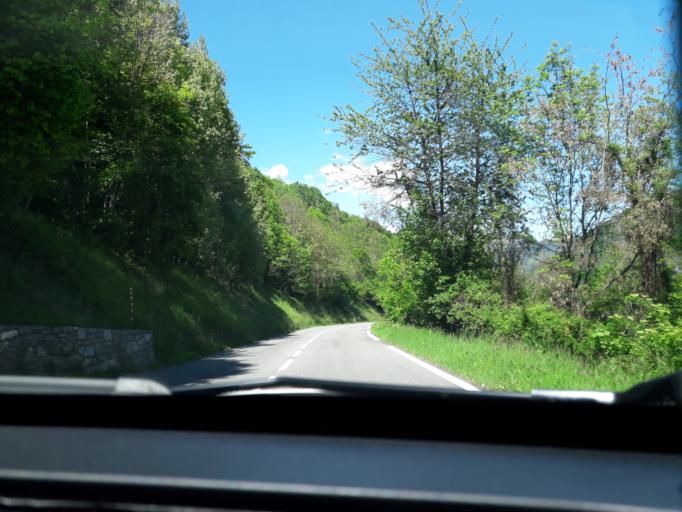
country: FR
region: Rhone-Alpes
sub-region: Departement de la Savoie
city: Salins-les-Thermes
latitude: 45.4588
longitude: 6.5132
